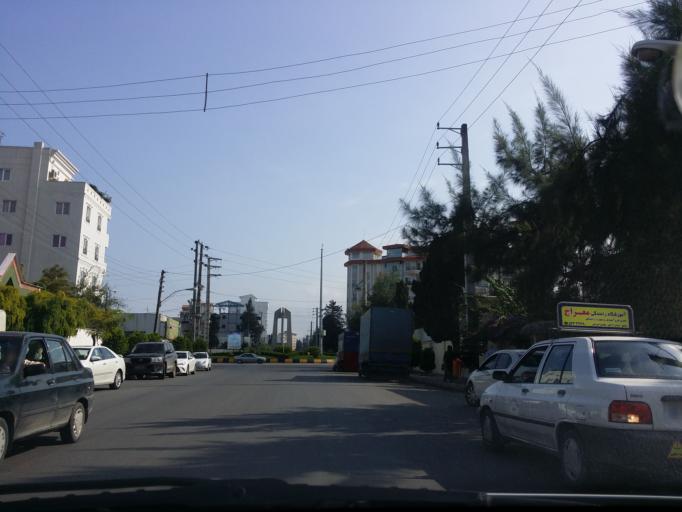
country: IR
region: Mazandaran
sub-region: Nowshahr
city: Nowshahr
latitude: 36.6481
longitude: 51.4920
